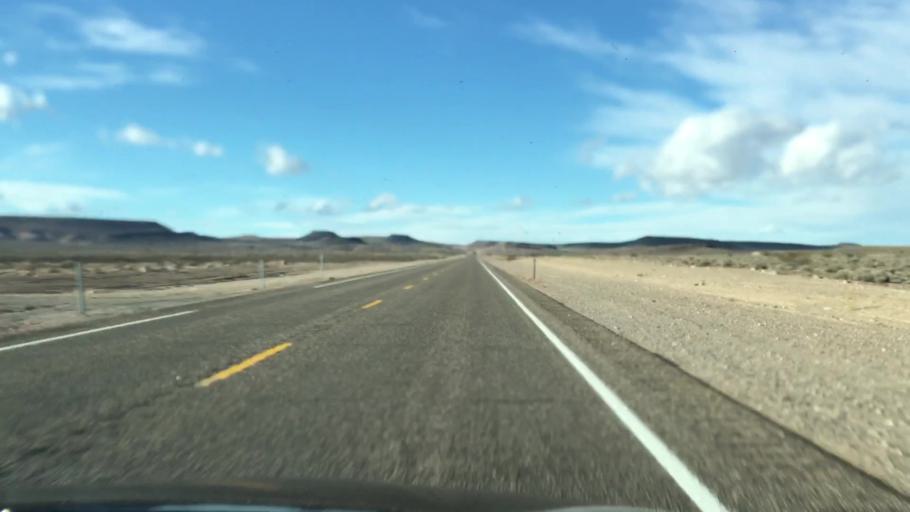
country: US
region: Nevada
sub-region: Esmeralda County
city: Goldfield
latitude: 37.3565
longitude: -117.1118
